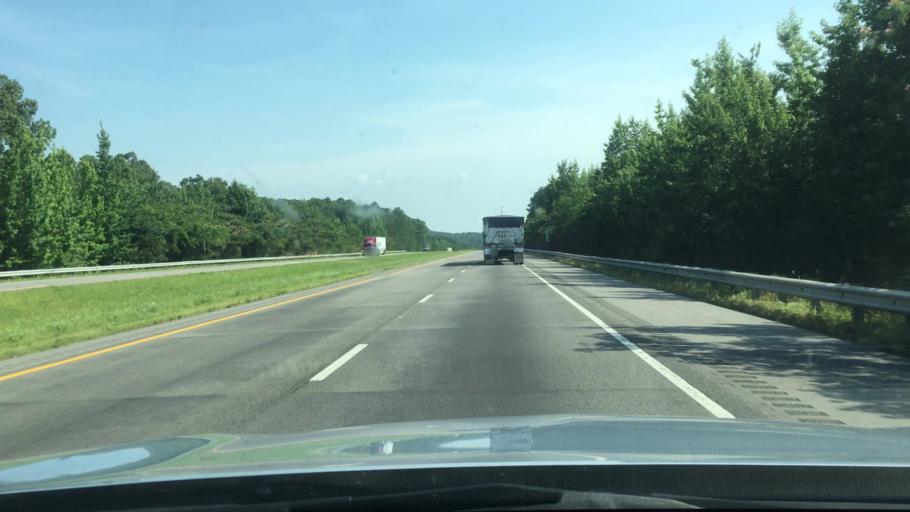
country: US
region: Alabama
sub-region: DeKalb County
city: Fort Payne
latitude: 34.5277
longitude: -85.6904
